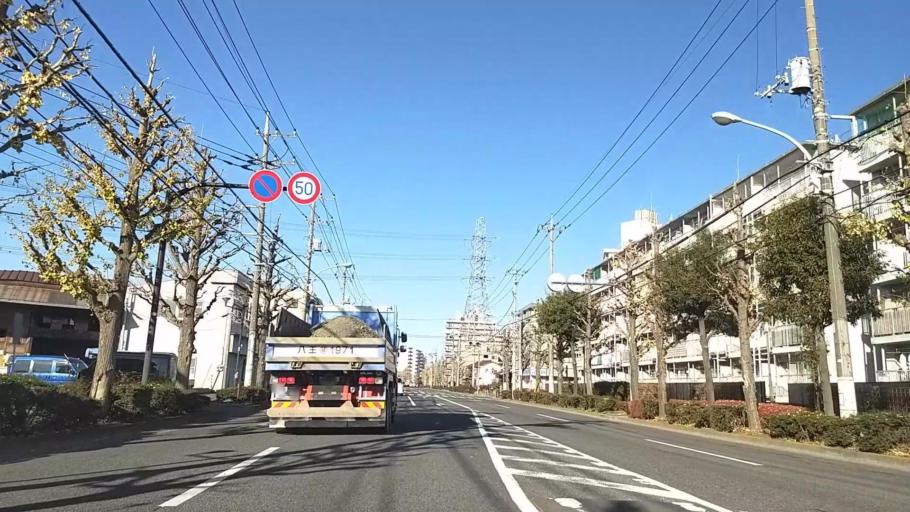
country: JP
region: Tokyo
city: Chofugaoka
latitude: 35.6445
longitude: 139.4995
